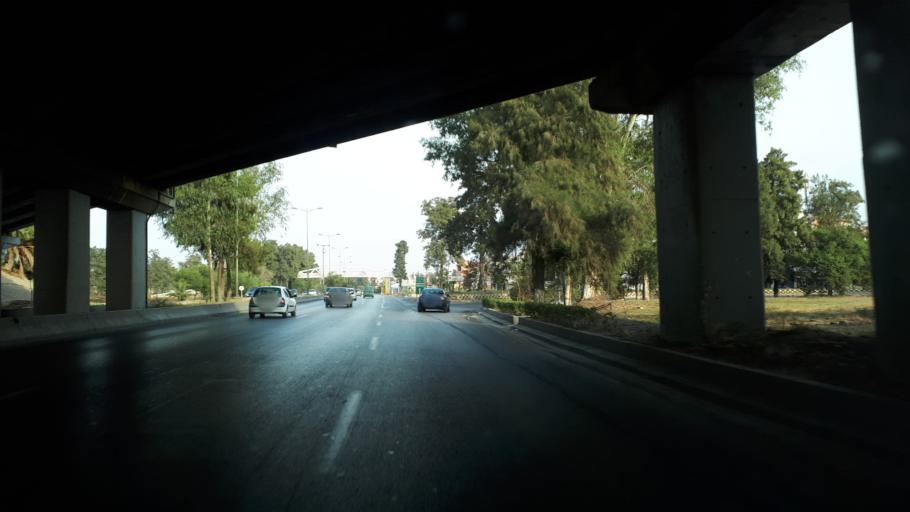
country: DZ
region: Alger
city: Dar el Beida
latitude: 36.7274
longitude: 3.2113
